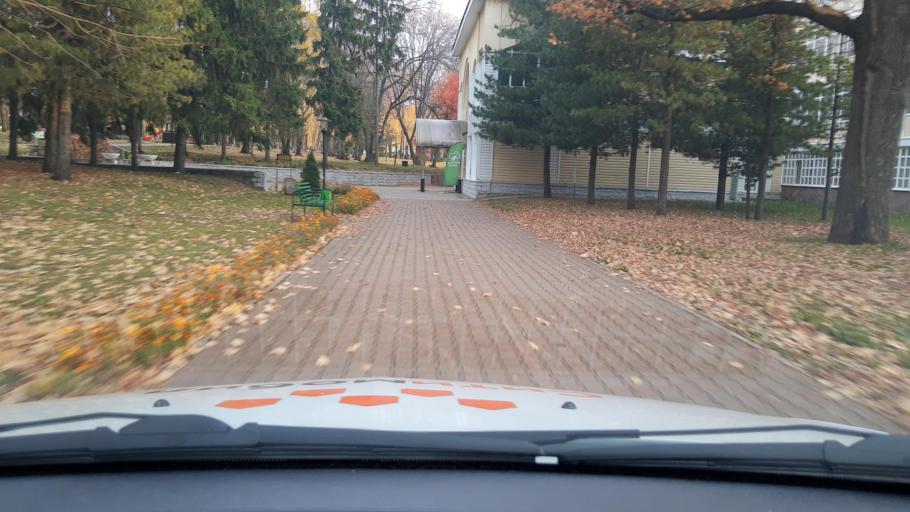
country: RU
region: Bashkortostan
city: Ufa
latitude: 54.7128
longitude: 56.0159
